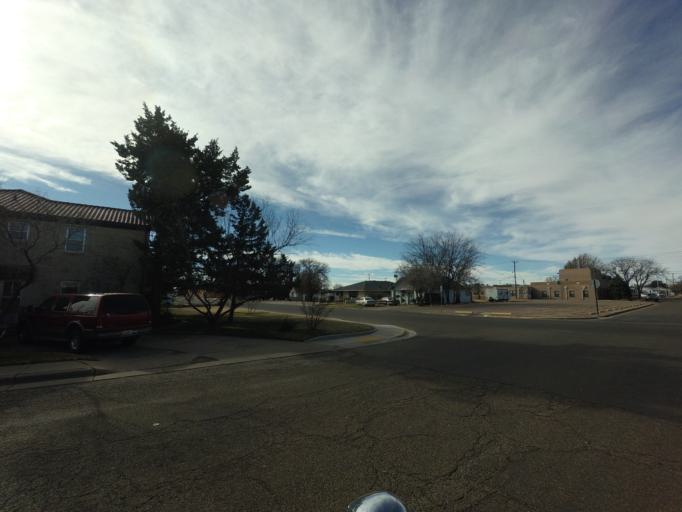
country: US
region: New Mexico
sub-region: Curry County
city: Clovis
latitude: 34.4099
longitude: -103.2038
